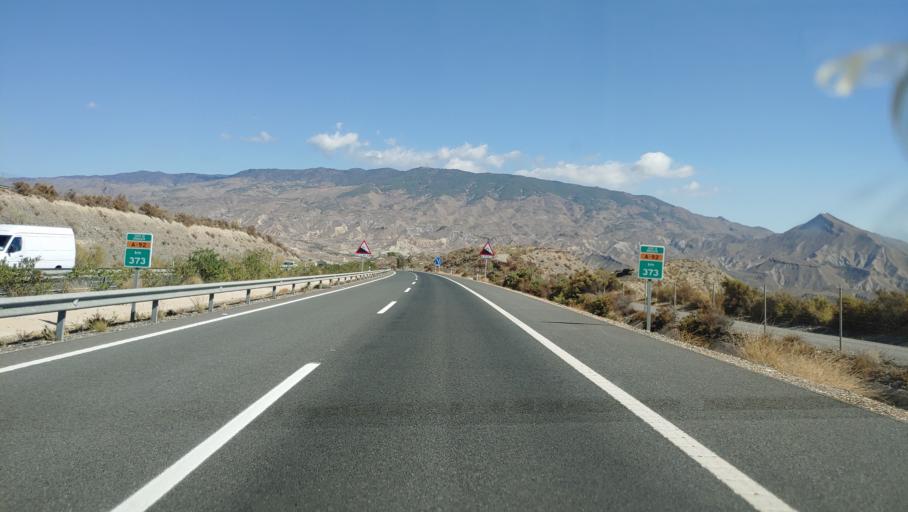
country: ES
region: Andalusia
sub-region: Provincia de Almeria
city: Tabernas
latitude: 37.0366
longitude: -2.4640
